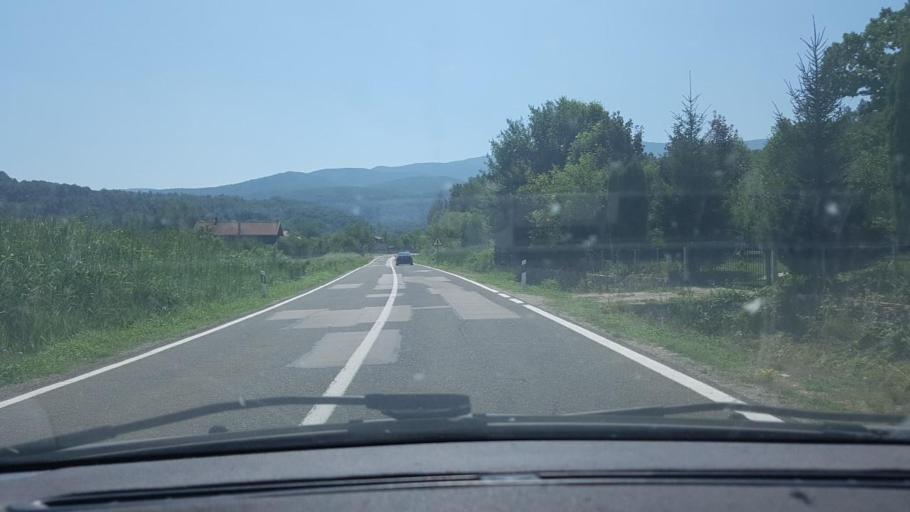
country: BA
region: Federation of Bosnia and Herzegovina
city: Bihac
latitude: 44.7533
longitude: 15.9416
